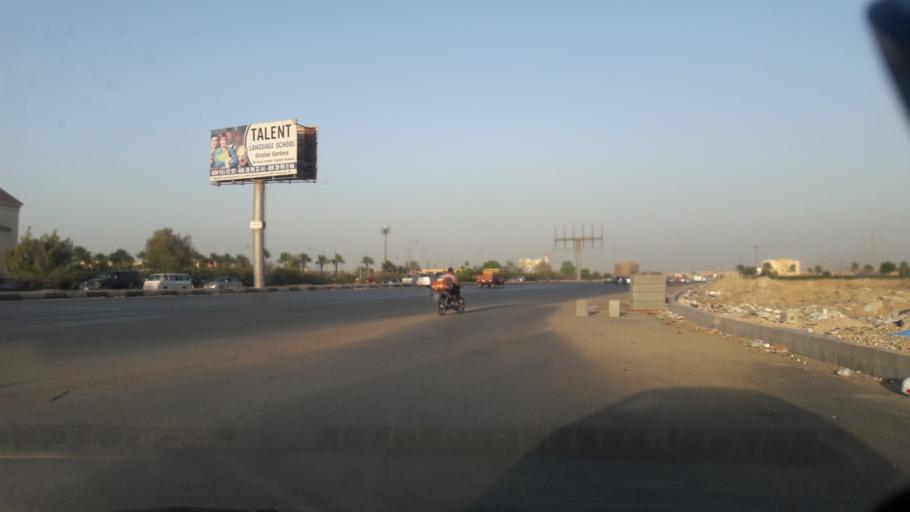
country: EG
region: Al Jizah
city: Madinat Sittah Uktubar
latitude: 29.9617
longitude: 31.0432
